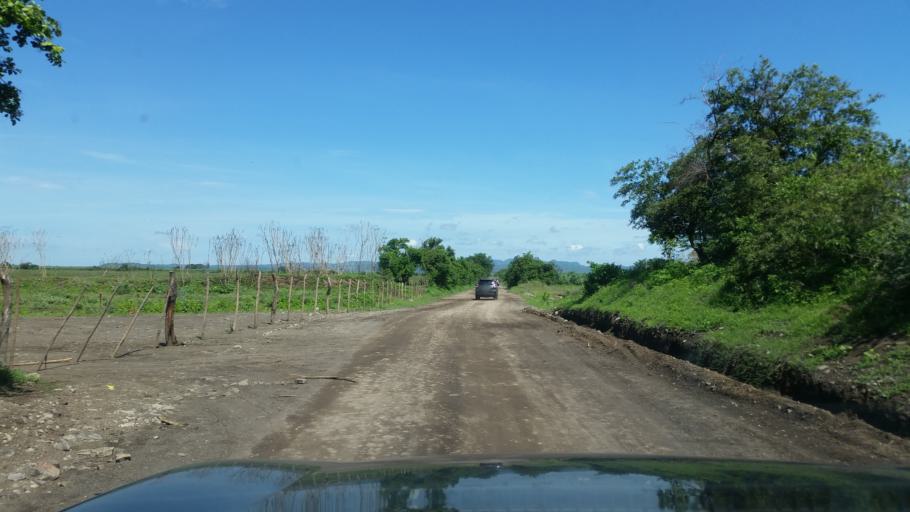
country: NI
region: Chinandega
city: Puerto Morazan
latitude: 12.7723
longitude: -87.0941
